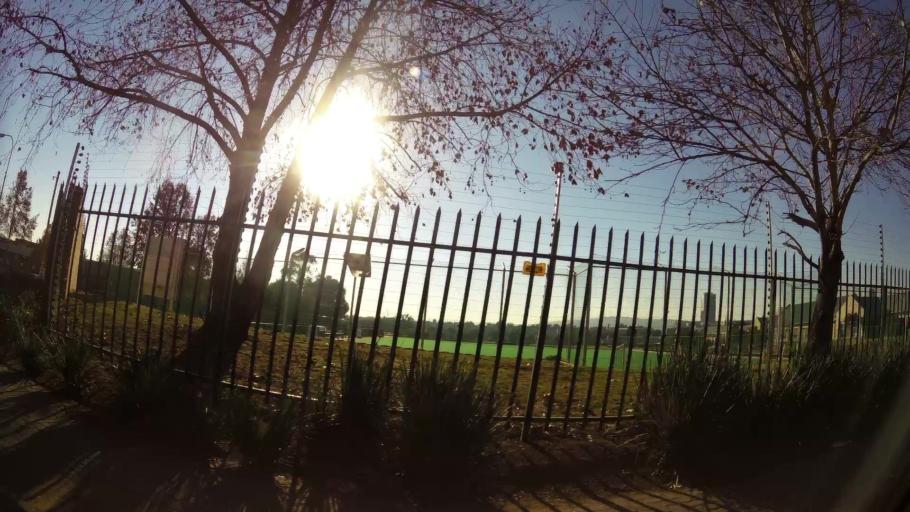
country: ZA
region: Gauteng
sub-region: City of Johannesburg Metropolitan Municipality
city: Johannesburg
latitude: -26.1872
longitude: 28.1140
